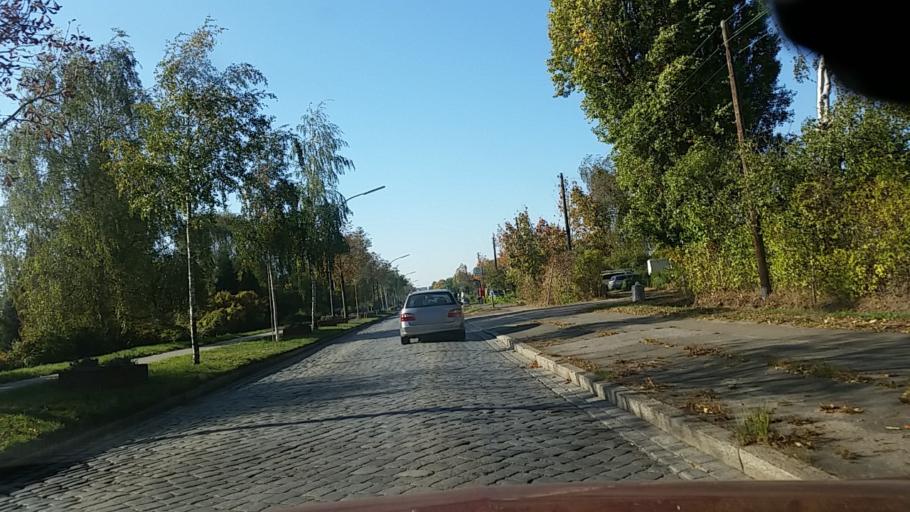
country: DE
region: Hamburg
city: Rothenburgsort
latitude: 53.5446
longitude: 10.0599
